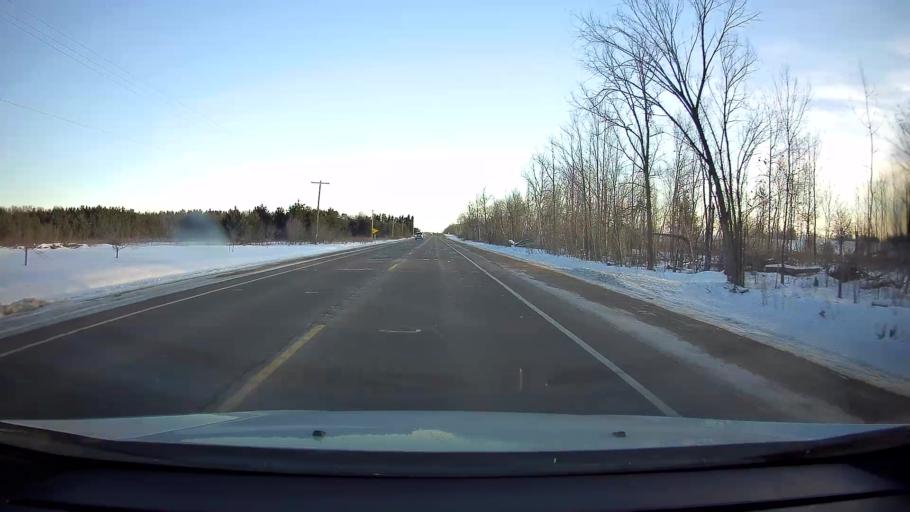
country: US
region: Wisconsin
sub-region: Barron County
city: Cumberland
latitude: 45.4840
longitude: -92.0666
